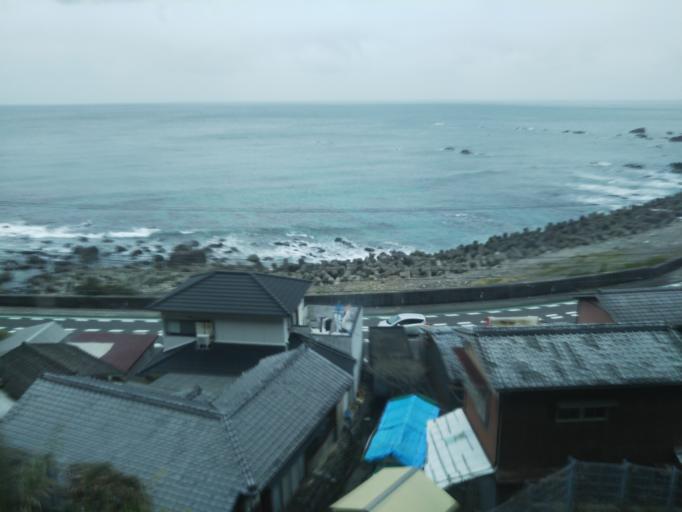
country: JP
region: Kochi
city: Nakamura
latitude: 33.0588
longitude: 133.0988
